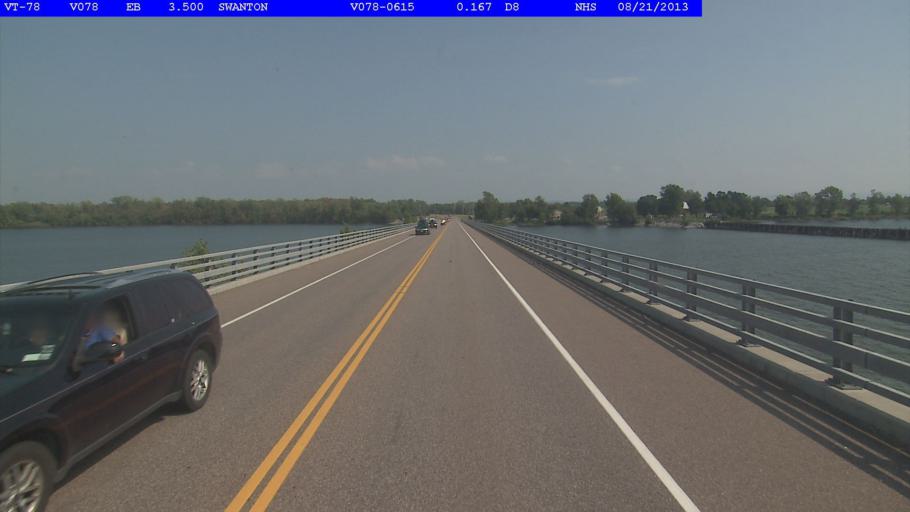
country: US
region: Vermont
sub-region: Franklin County
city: Swanton
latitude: 44.9720
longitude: -73.2173
